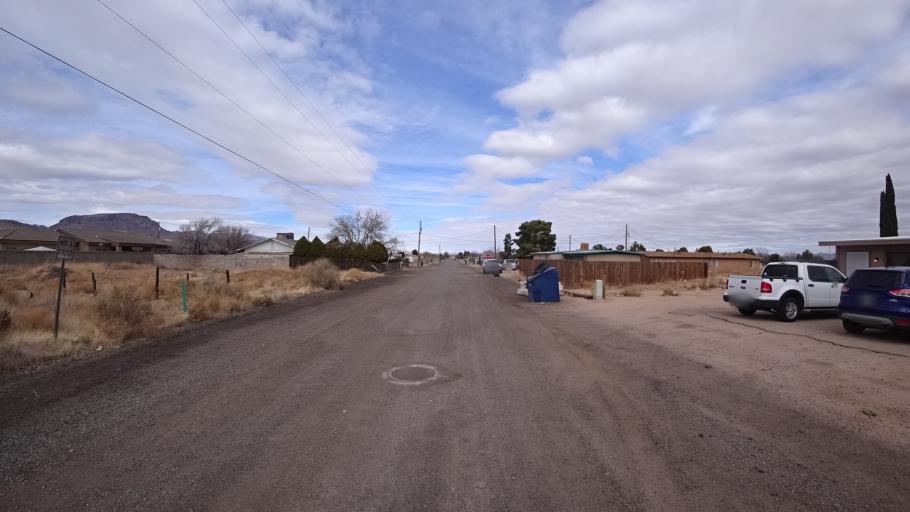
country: US
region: Arizona
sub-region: Mohave County
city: New Kingman-Butler
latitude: 35.2351
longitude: -114.0200
